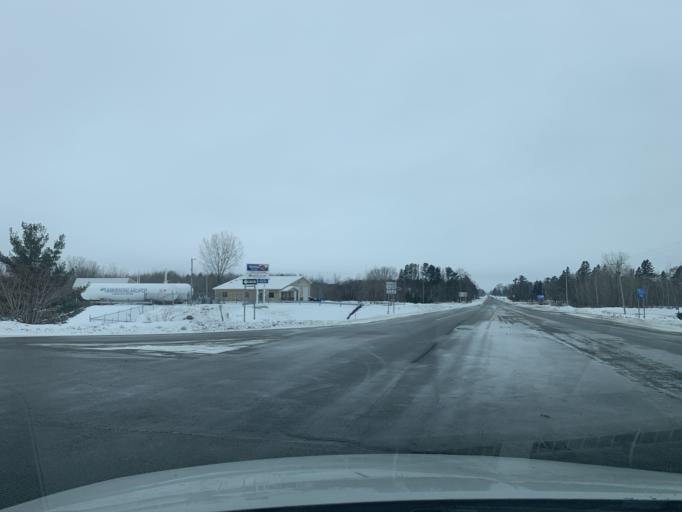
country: US
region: Minnesota
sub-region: Pine County
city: Rock Creek
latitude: 45.7668
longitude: -92.9908
